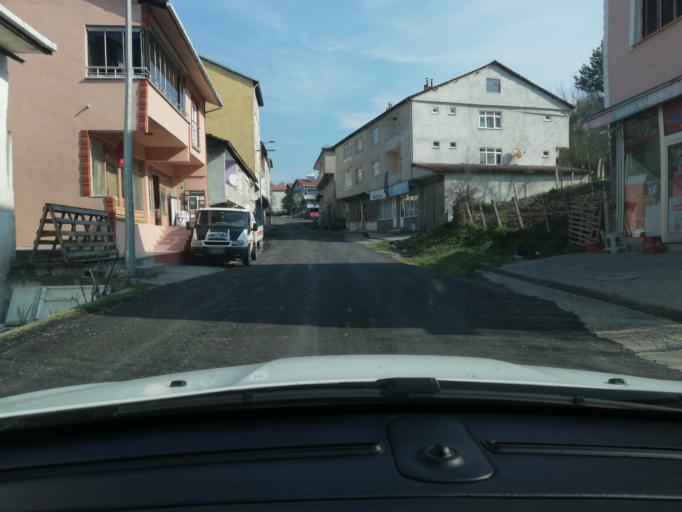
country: TR
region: Karabuk
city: Yenice
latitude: 41.2621
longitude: 32.3638
